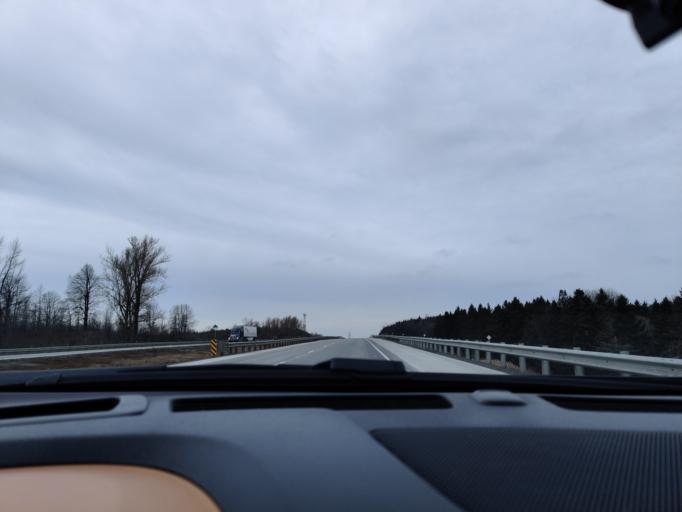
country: CA
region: Ontario
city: Cornwall
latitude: 45.0668
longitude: -74.6556
